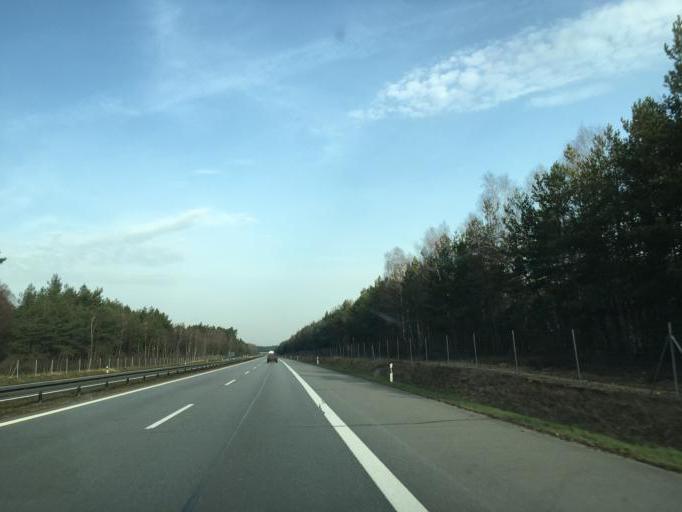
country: DE
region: Brandenburg
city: Wittstock
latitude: 53.0973
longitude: 12.5002
